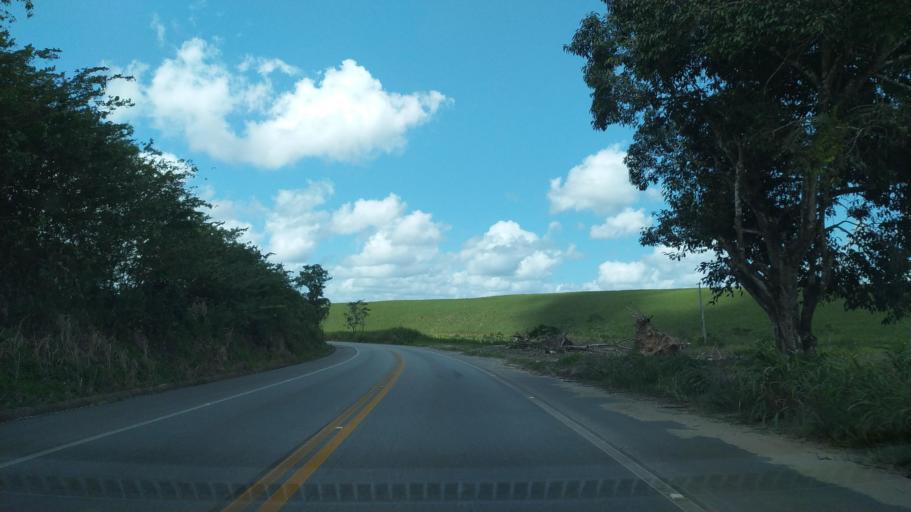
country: BR
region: Alagoas
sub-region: Messias
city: Messias
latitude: -9.3705
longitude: -35.8449
